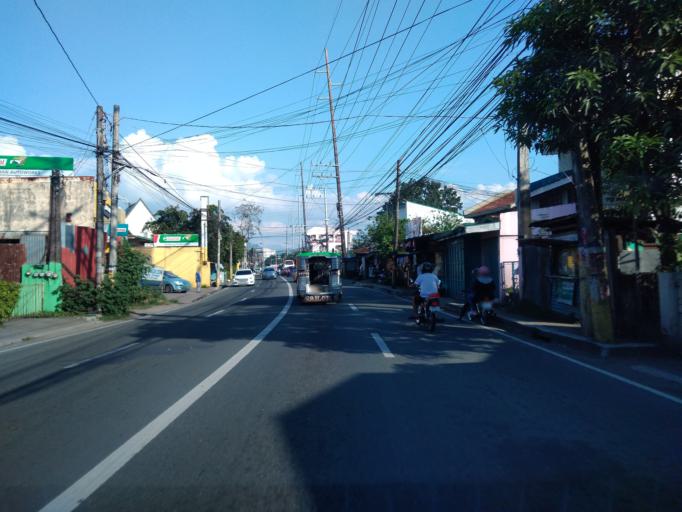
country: PH
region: Calabarzon
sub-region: Province of Laguna
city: Los Banos
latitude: 14.1800
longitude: 121.2353
